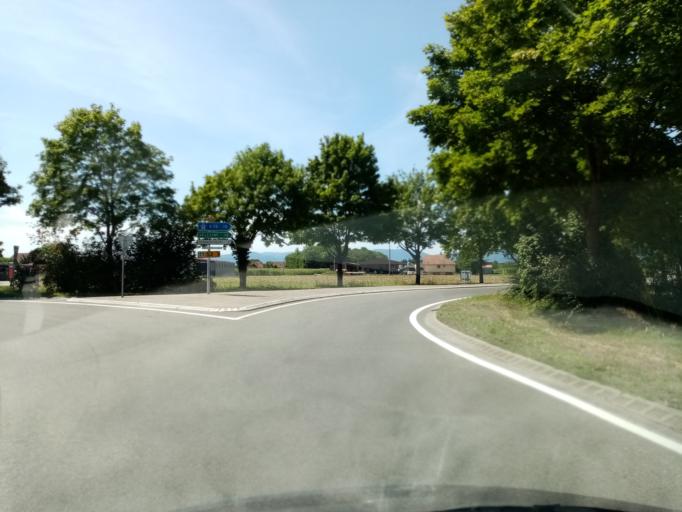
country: FR
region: Alsace
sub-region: Departement du Bas-Rhin
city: Mussig
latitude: 48.2038
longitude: 7.5213
